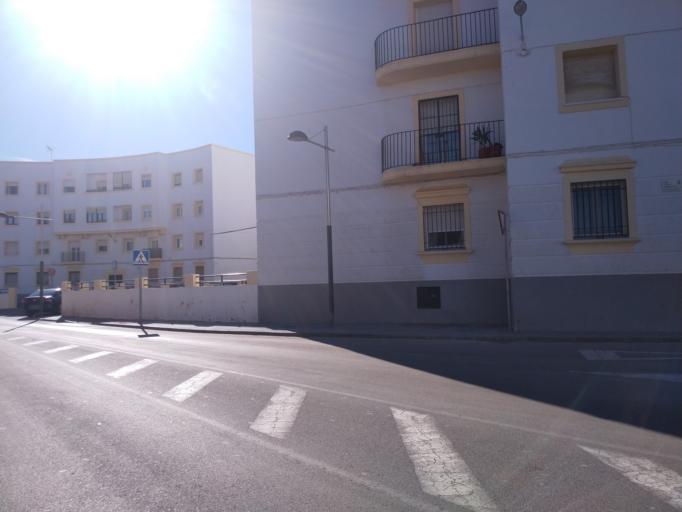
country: ES
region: Andalusia
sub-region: Provincia de Cadiz
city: San Fernando
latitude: 36.4779
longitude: -6.1951
